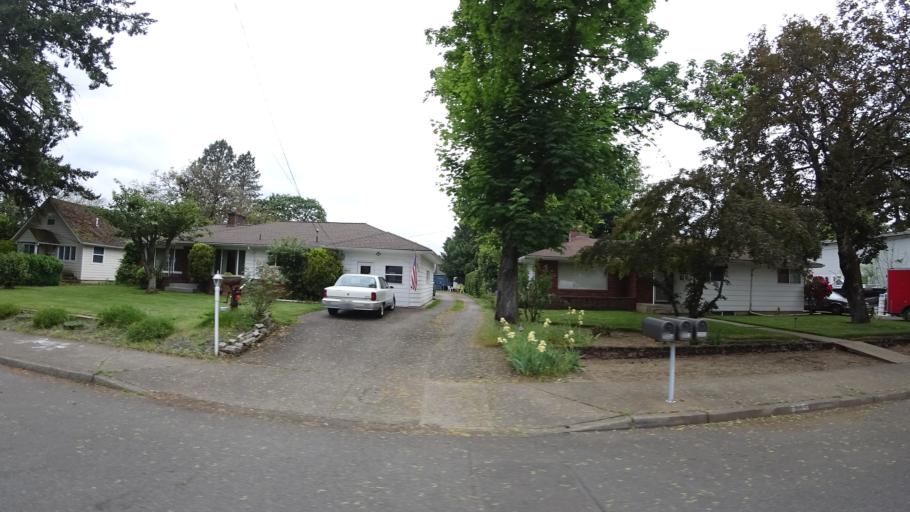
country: US
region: Oregon
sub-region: Multnomah County
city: Lents
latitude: 45.5086
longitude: -122.5210
